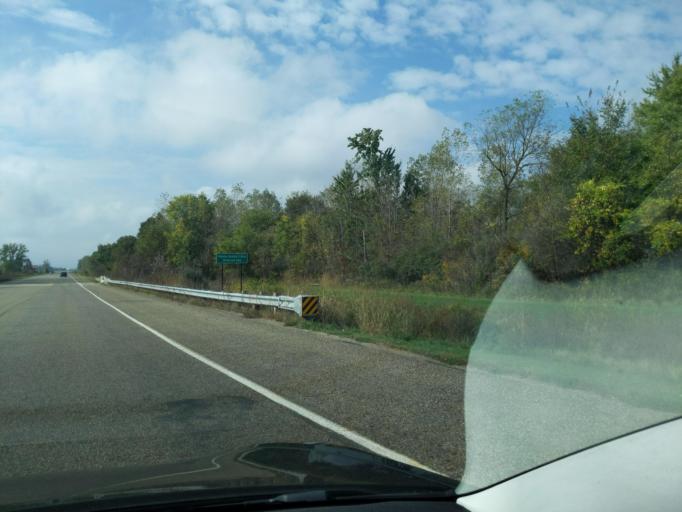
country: US
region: Michigan
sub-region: Eaton County
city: Potterville
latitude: 42.6167
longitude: -84.7506
